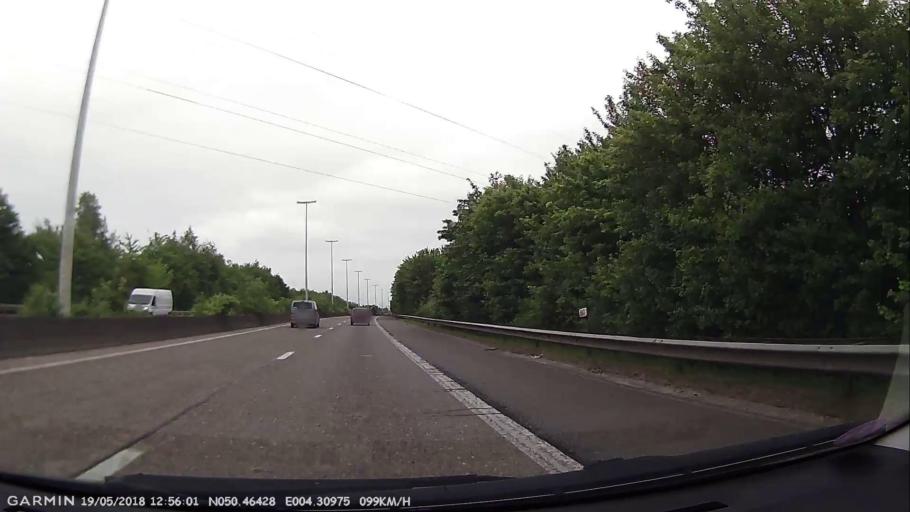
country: BE
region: Wallonia
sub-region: Province du Hainaut
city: Chapelle-lez-Herlaimont
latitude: 50.4645
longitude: 4.3099
